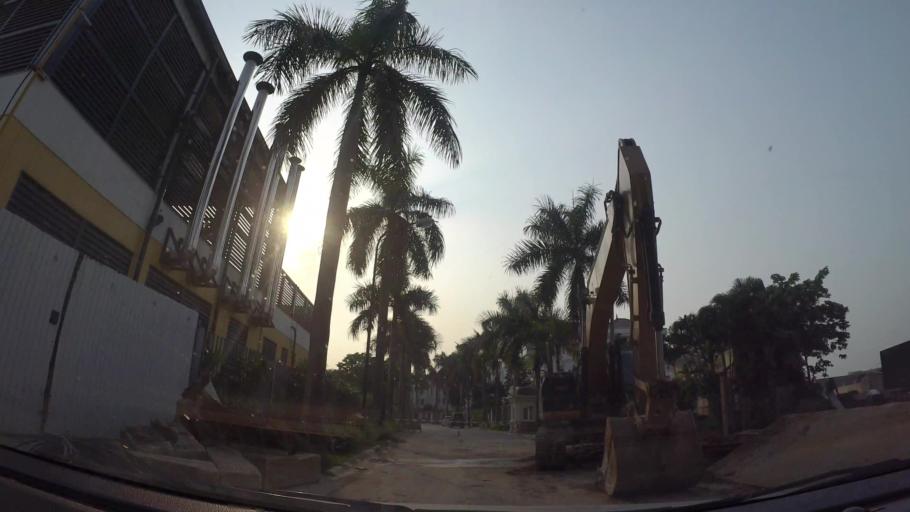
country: VN
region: Ha Noi
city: Tay Ho
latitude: 21.0766
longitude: 105.8075
